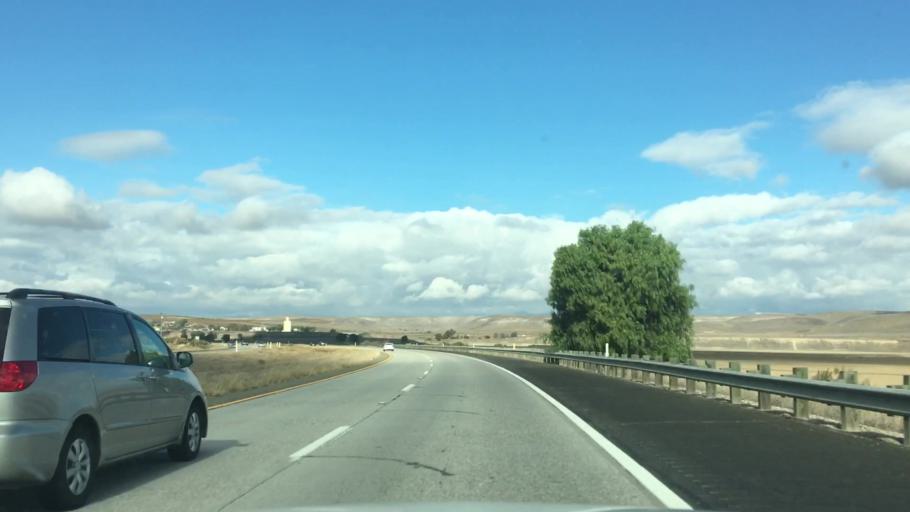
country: US
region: California
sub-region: Monterey County
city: King City
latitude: 36.1127
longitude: -121.0196
